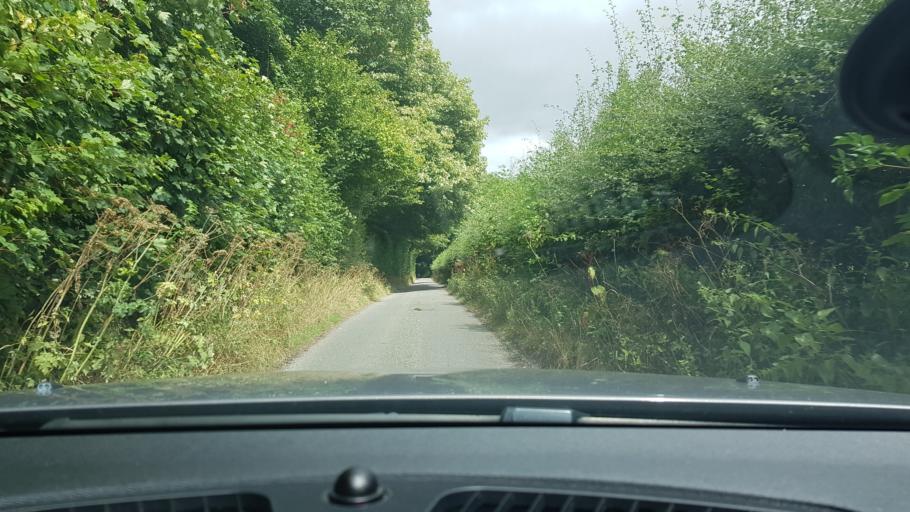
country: GB
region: England
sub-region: West Berkshire
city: Hungerford
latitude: 51.4377
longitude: -1.5166
